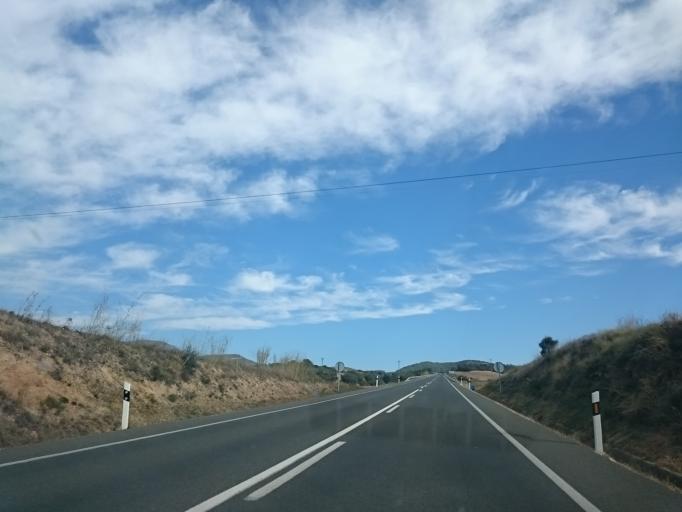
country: ES
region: Aragon
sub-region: Provincia de Huesca
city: Baells
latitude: 41.9521
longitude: 0.4650
